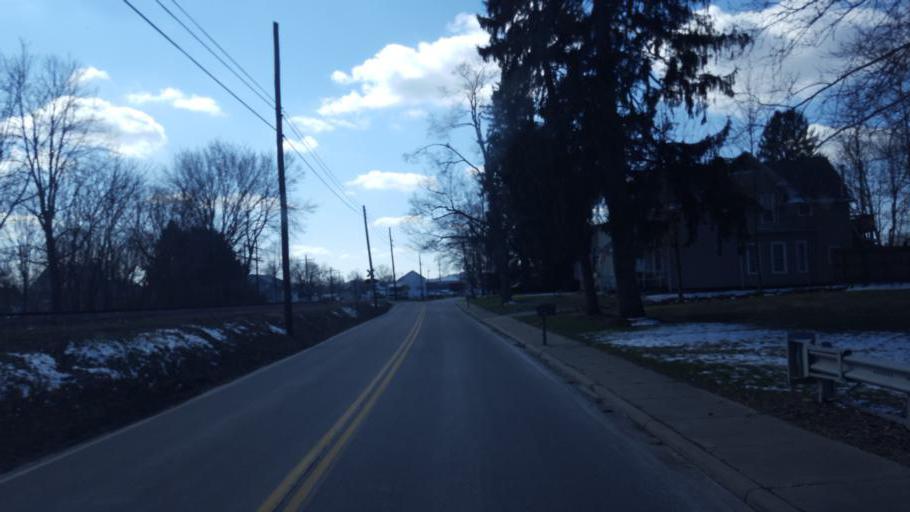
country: US
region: Ohio
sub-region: Licking County
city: Utica
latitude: 40.2409
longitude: -82.4523
